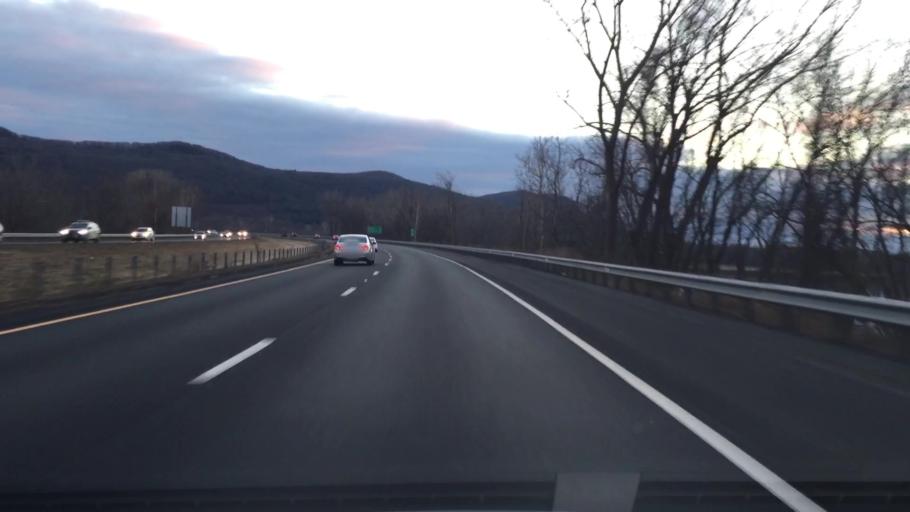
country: US
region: Massachusetts
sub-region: Hampshire County
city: Northampton
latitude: 42.2984
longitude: -72.6299
